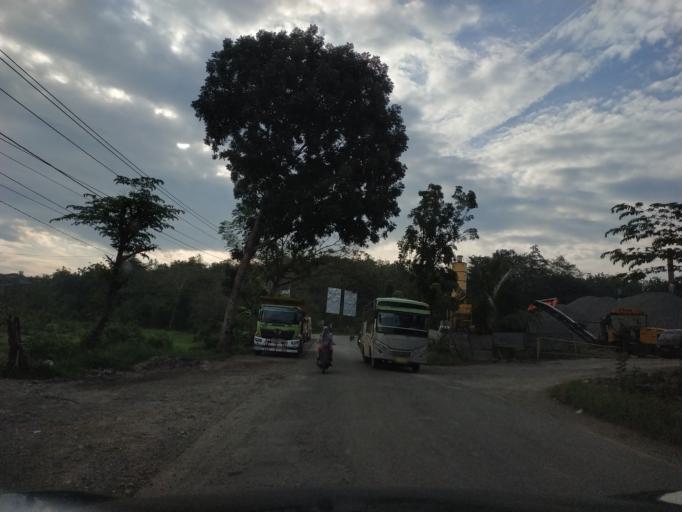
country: ID
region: Central Java
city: Ngampel
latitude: -6.9003
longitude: 111.4404
